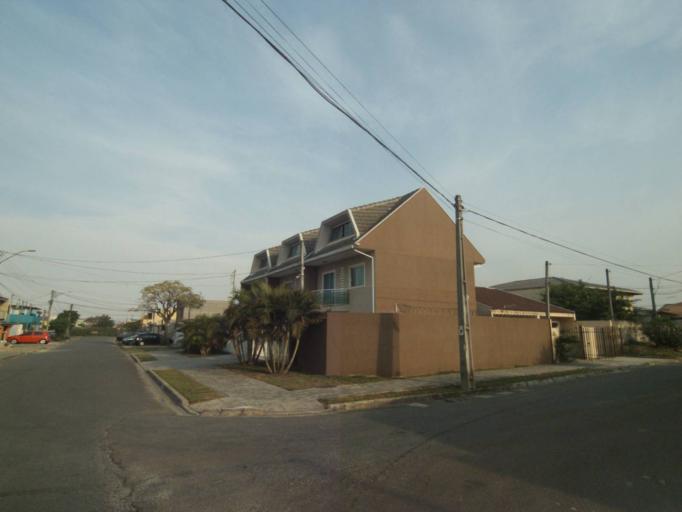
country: BR
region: Parana
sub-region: Pinhais
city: Pinhais
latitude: -25.4809
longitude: -49.2011
